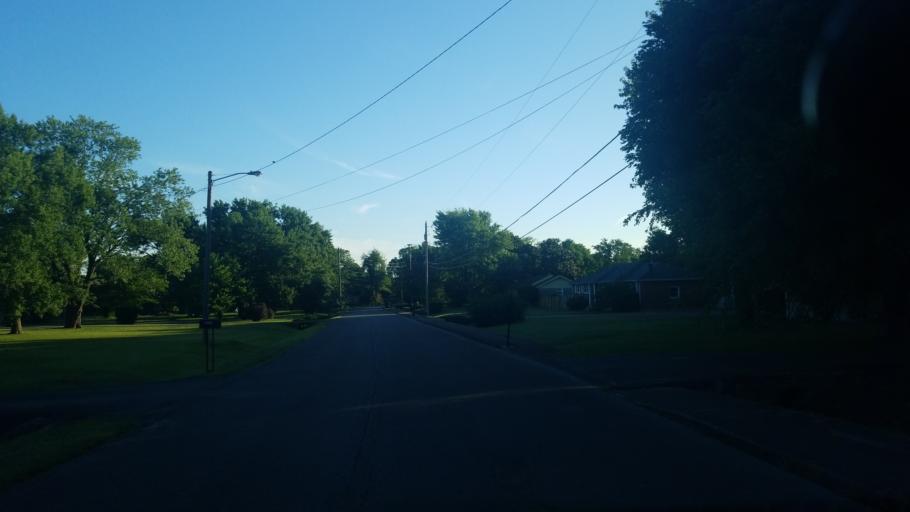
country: US
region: Tennessee
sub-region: Davidson County
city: Nashville
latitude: 36.2261
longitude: -86.7712
